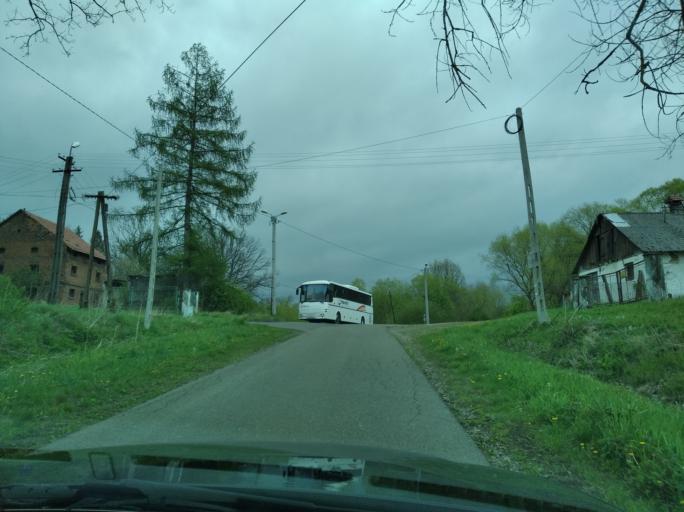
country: PL
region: Subcarpathian Voivodeship
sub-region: Powiat brzozowski
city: Dydnia
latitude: 49.6682
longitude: 22.2519
